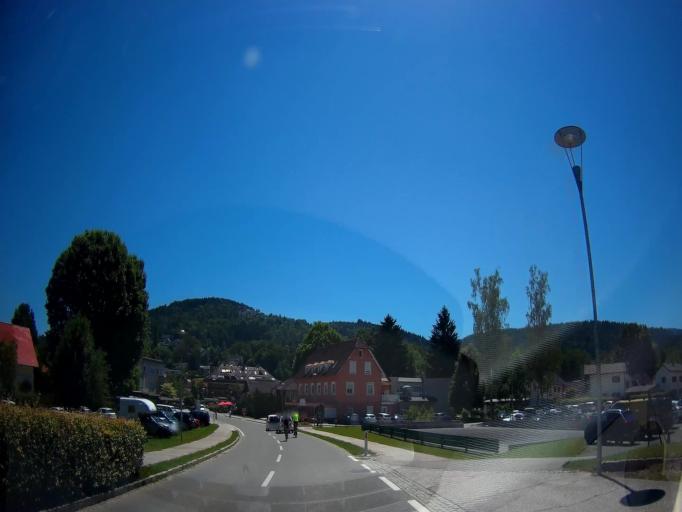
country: AT
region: Carinthia
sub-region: Politischer Bezirk Klagenfurt Land
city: Keutschach am See
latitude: 46.6077
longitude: 14.1795
